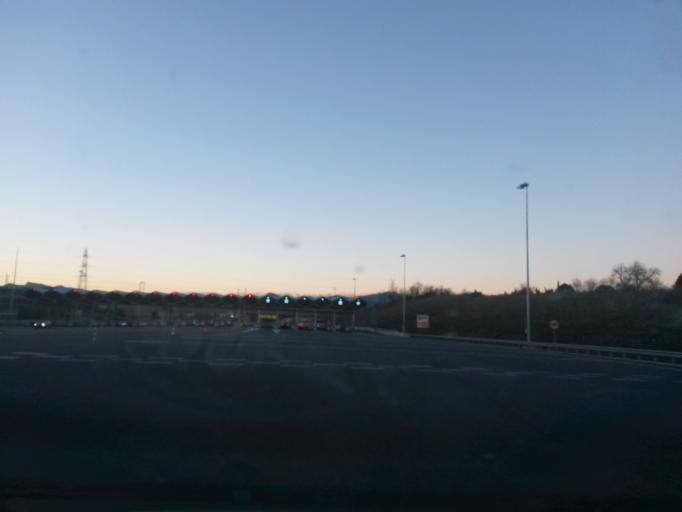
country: ES
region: Catalonia
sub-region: Provincia de Girona
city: Fornells de la Selva
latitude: 41.9276
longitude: 2.7917
